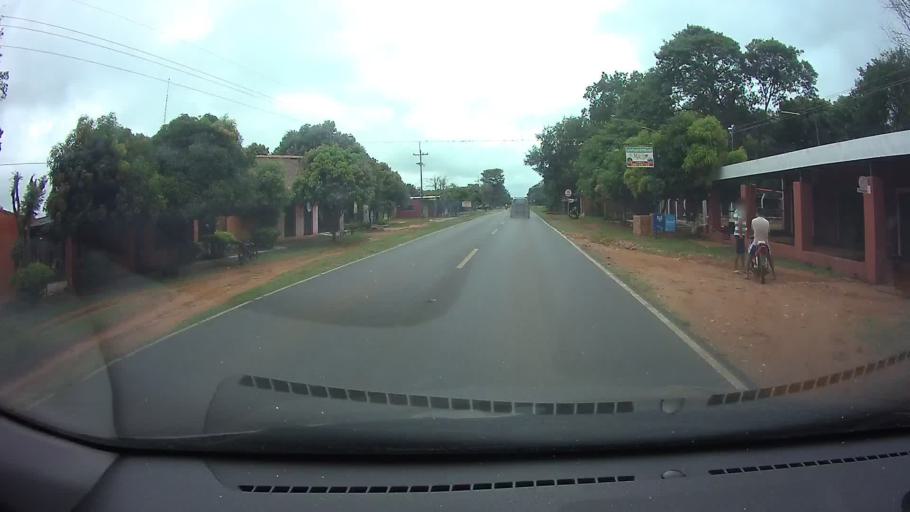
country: PY
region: Central
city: Nueva Italia
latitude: -25.5777
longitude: -57.5054
